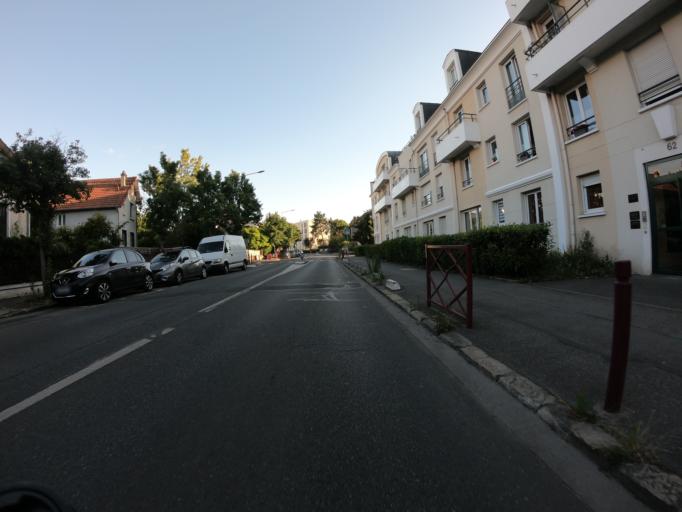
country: FR
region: Ile-de-France
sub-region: Departement du Val-de-Marne
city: Fresnes
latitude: 48.7557
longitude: 2.3138
